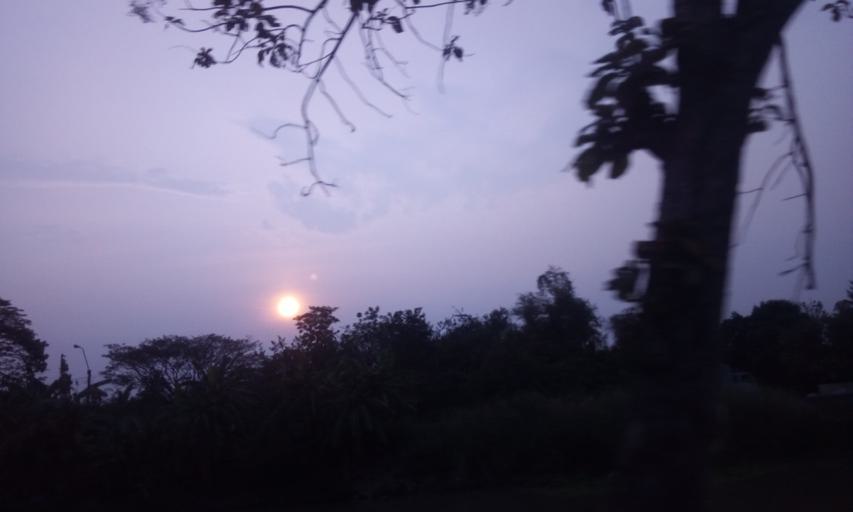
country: TH
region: Bangkok
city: Nong Chok
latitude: 13.8883
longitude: 100.8865
